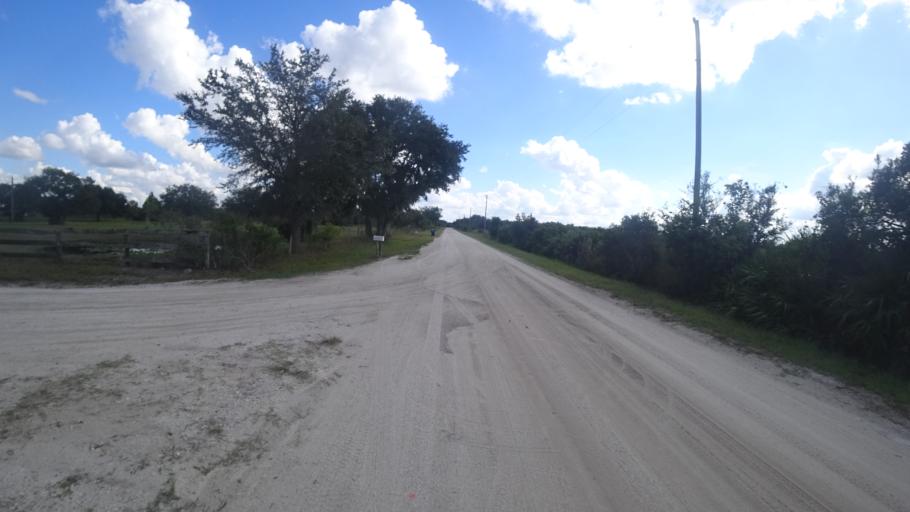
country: US
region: Florida
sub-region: Hillsborough County
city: Wimauma
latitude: 27.4311
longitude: -82.1486
